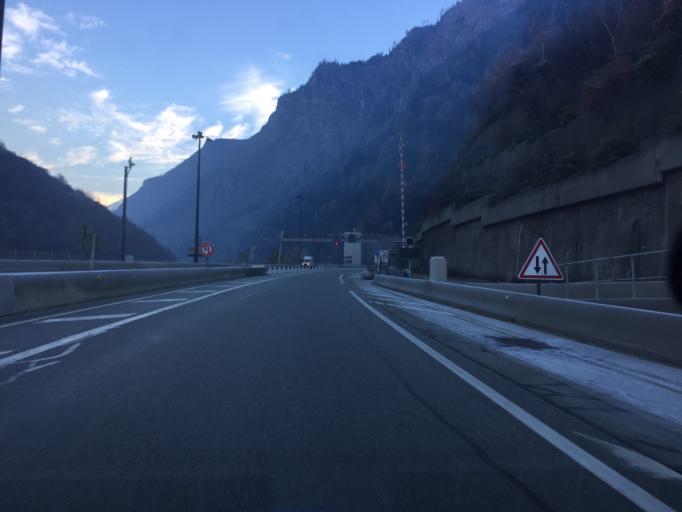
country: FR
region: Rhone-Alpes
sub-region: Departement de la Savoie
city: Saint-Michel-de-Maurienne
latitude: 45.2094
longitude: 6.5161
